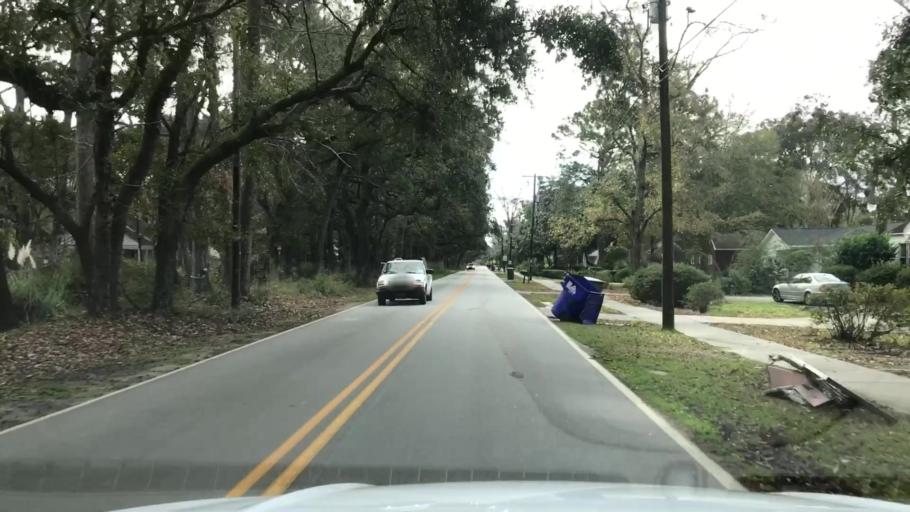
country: US
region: South Carolina
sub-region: Charleston County
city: North Charleston
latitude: 32.7836
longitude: -80.0201
